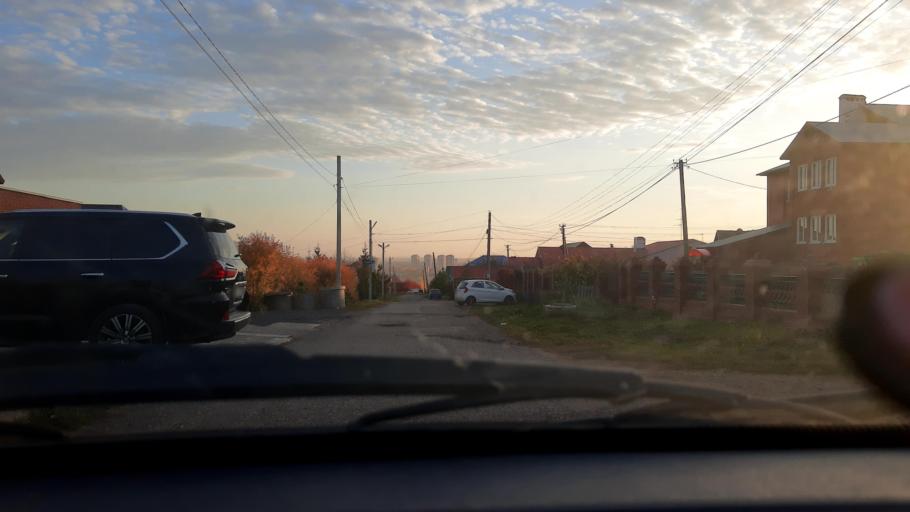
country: RU
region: Bashkortostan
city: Mikhaylovka
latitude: 54.8138
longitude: 55.8893
